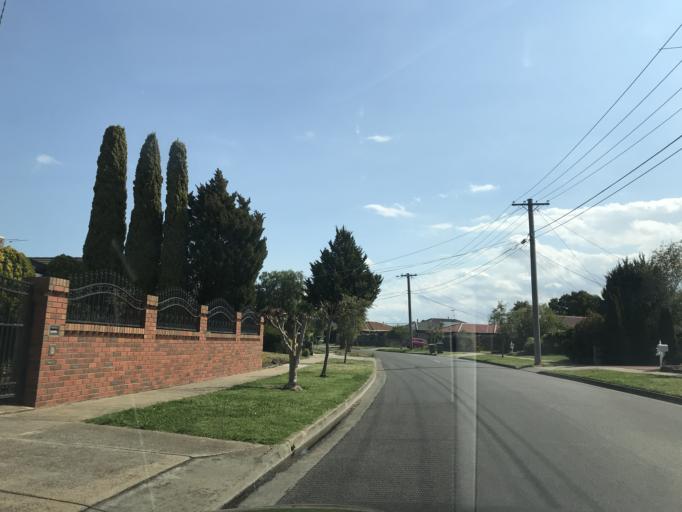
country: AU
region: Victoria
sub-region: Wyndham
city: Hoppers Crossing
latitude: -37.8692
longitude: 144.7133
